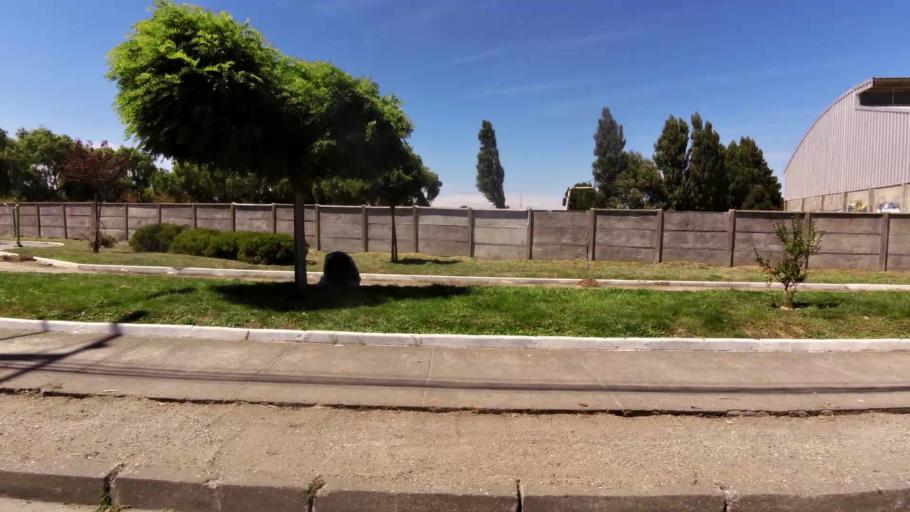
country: CL
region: Biobio
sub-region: Provincia de Concepcion
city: Talcahuano
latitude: -36.7571
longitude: -73.0828
